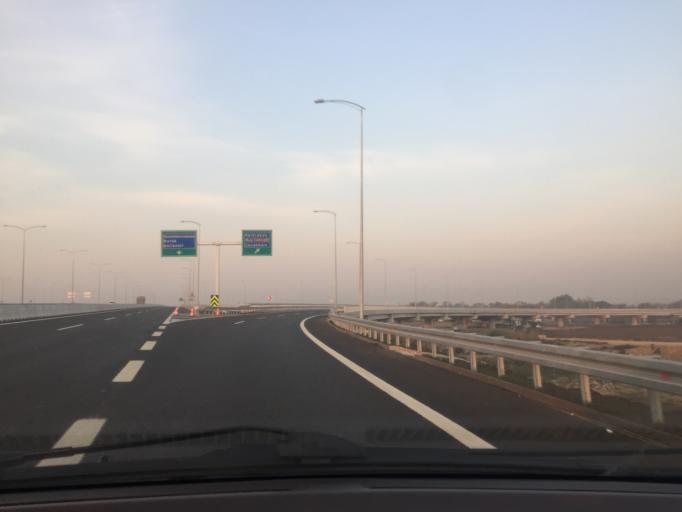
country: TR
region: Bursa
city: Karacabey
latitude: 40.1948
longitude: 28.3568
